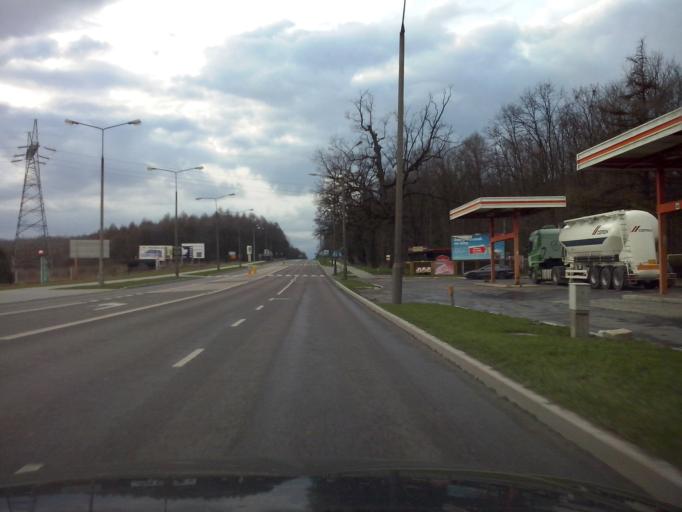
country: PL
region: Lublin Voivodeship
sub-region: Chelm
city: Chelm
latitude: 51.1489
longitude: 23.4291
